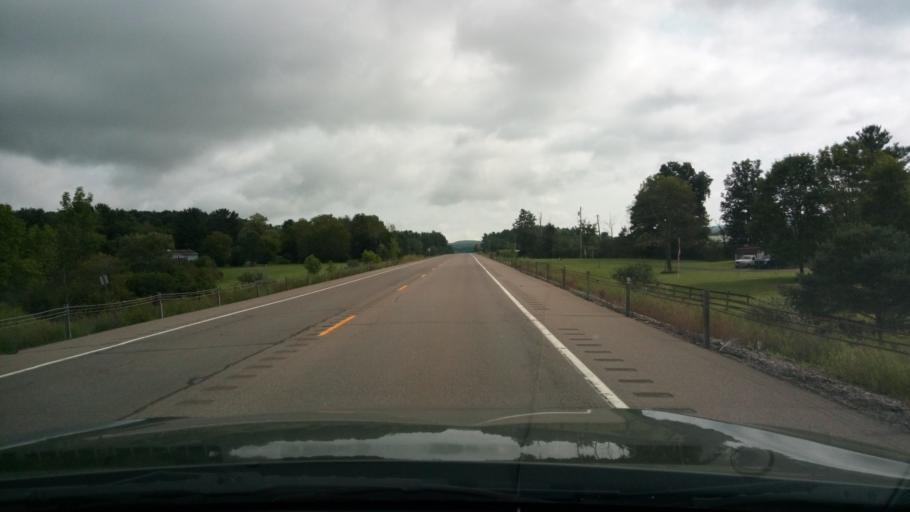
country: US
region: New York
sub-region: Chemung County
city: Horseheads North
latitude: 42.2014
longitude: -76.7807
